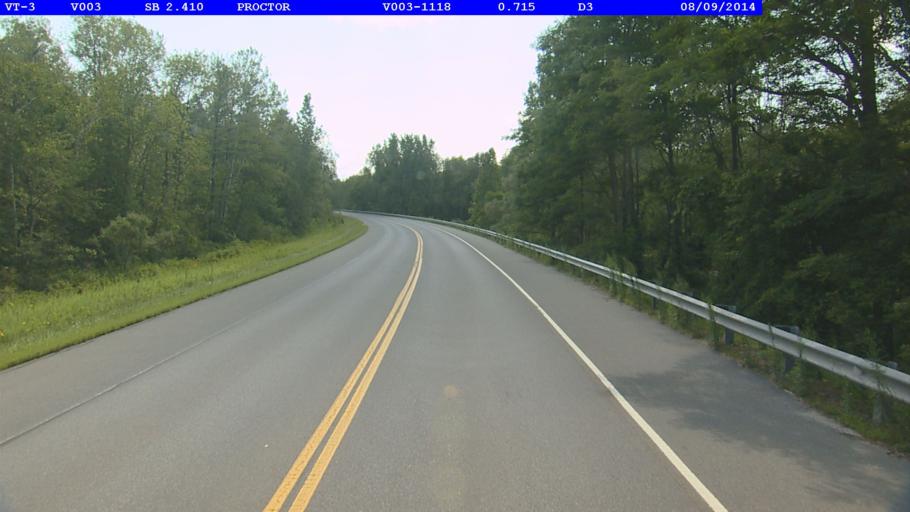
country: US
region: Vermont
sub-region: Rutland County
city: West Rutland
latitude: 43.6343
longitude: -73.0349
